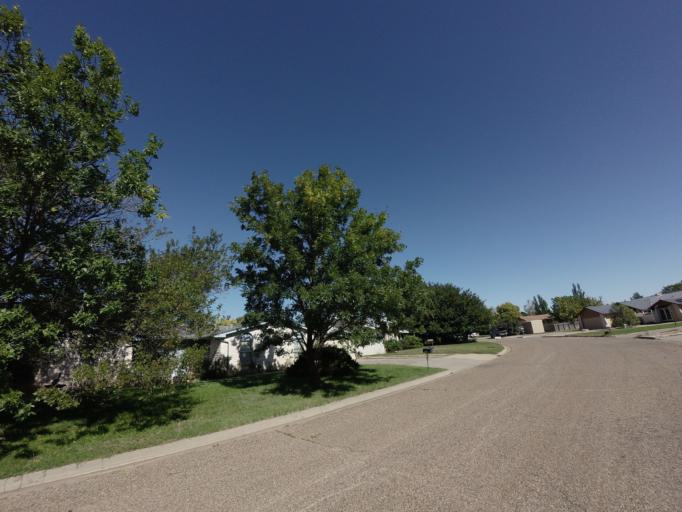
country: US
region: New Mexico
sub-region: Curry County
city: Clovis
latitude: 34.4252
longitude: -103.1852
